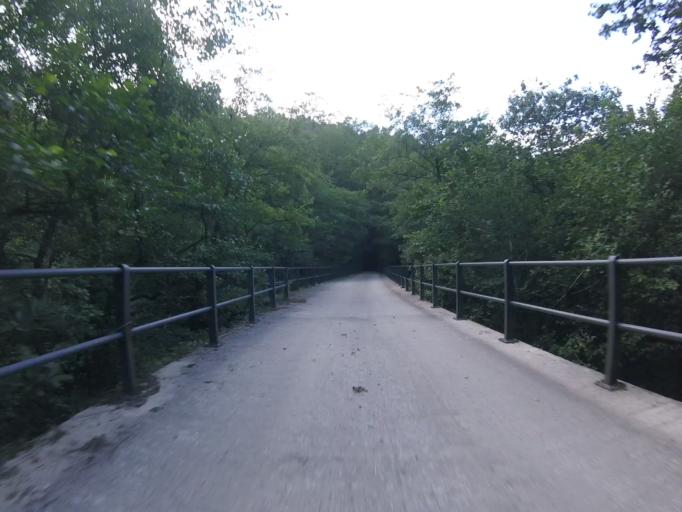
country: ES
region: Basque Country
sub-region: Provincia de Guipuzcoa
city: Berastegui
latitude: 43.1494
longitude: -1.9560
